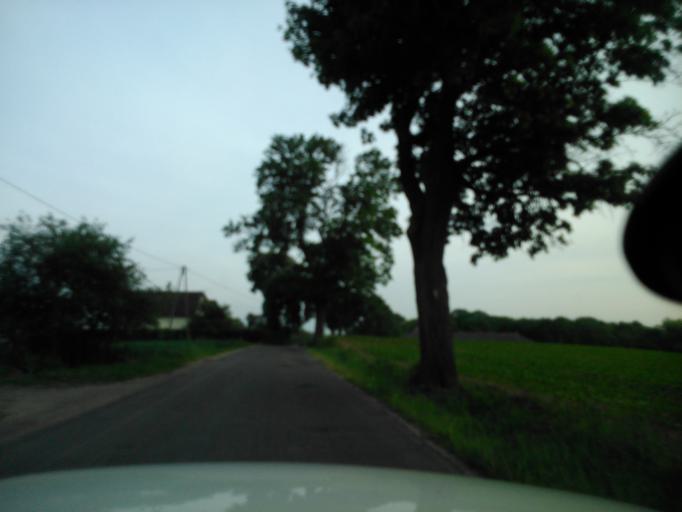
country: PL
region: Kujawsko-Pomorskie
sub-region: Powiat golubsko-dobrzynski
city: Kowalewo Pomorskie
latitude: 53.1209
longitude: 18.9134
